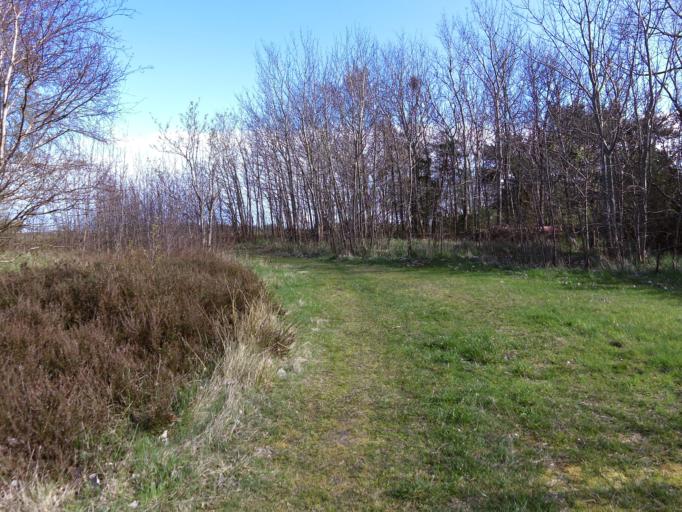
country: DE
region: Mecklenburg-Vorpommern
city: Hiddensee
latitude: 54.5578
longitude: 13.1013
